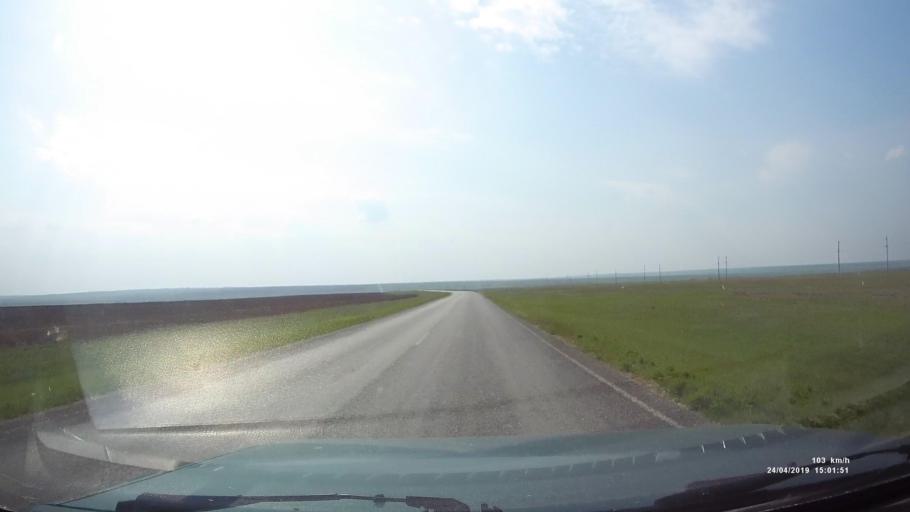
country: RU
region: Rostov
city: Remontnoye
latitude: 46.5666
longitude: 43.5250
